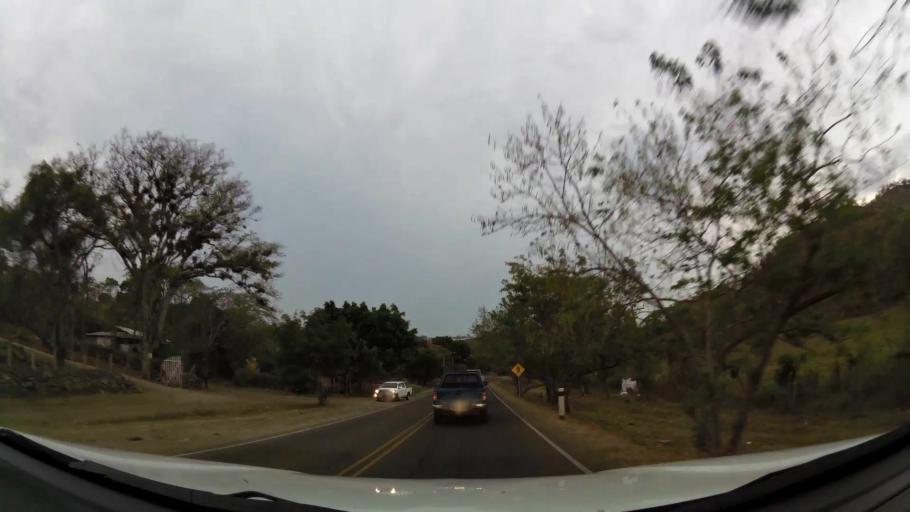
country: NI
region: Esteli
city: Esteli
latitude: 13.0017
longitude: -86.3062
